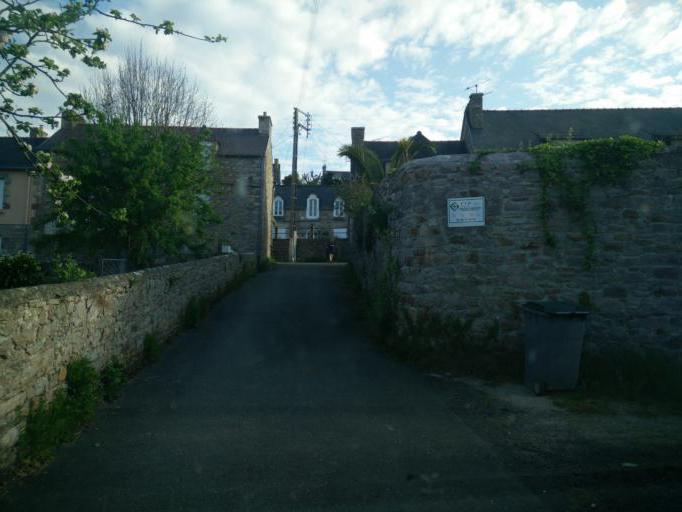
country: FR
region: Brittany
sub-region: Departement des Cotes-d'Armor
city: Erquy
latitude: 48.6384
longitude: -2.4660
